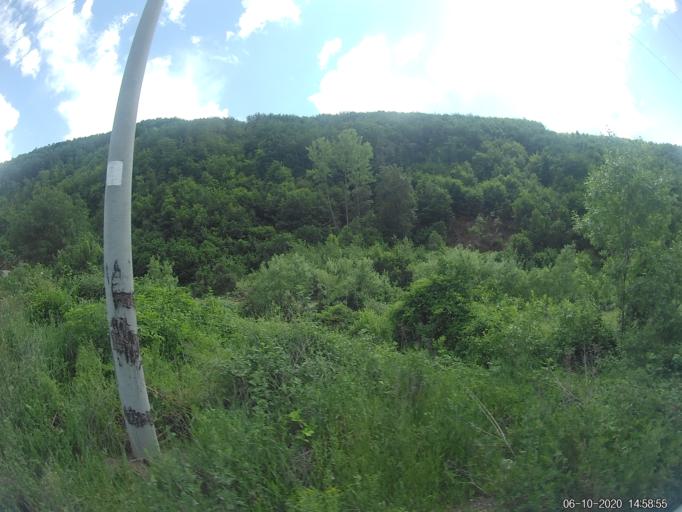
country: XK
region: Ferizaj
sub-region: Komuna e Shtimes
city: Shtime
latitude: 42.4129
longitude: 21.0194
